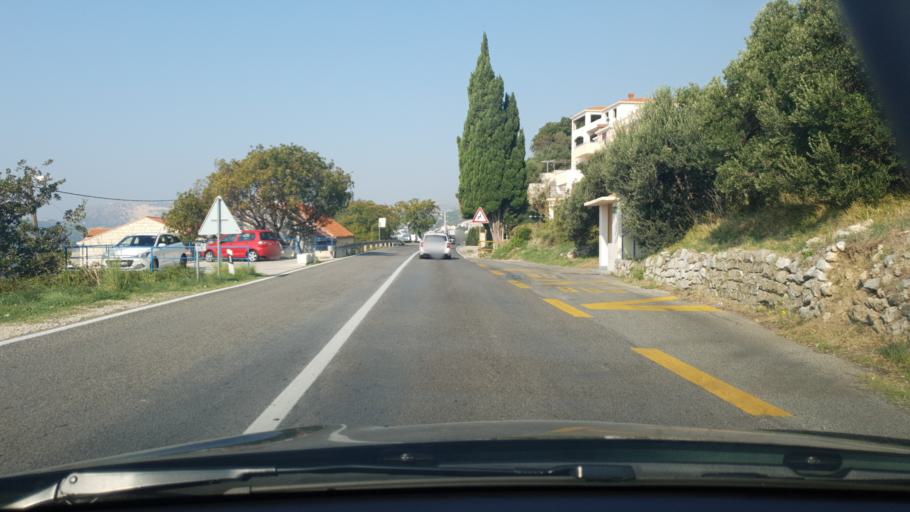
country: HR
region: Dubrovacko-Neretvanska
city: Cavtat
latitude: 42.6165
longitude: 18.2168
